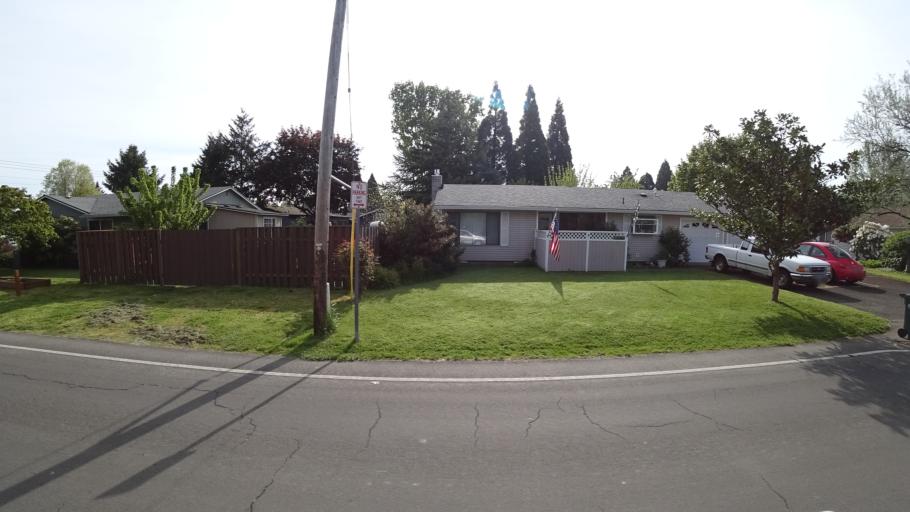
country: US
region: Oregon
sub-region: Washington County
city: Hillsboro
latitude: 45.5362
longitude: -122.9646
